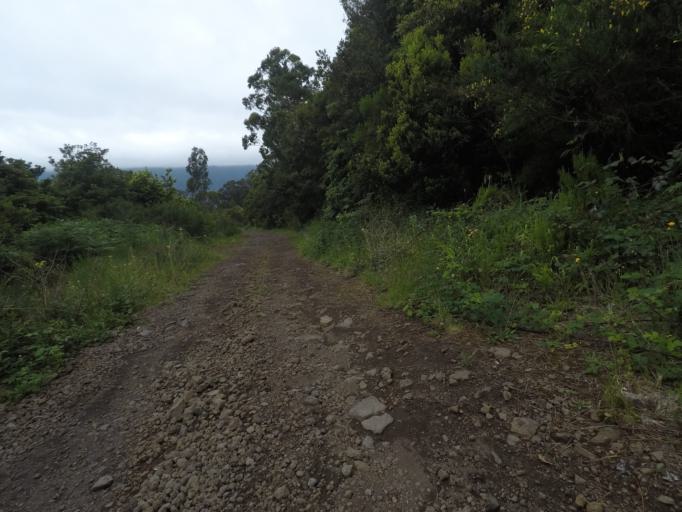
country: PT
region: Madeira
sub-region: Sao Vicente
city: Sao Vicente
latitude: 32.7758
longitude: -17.0533
